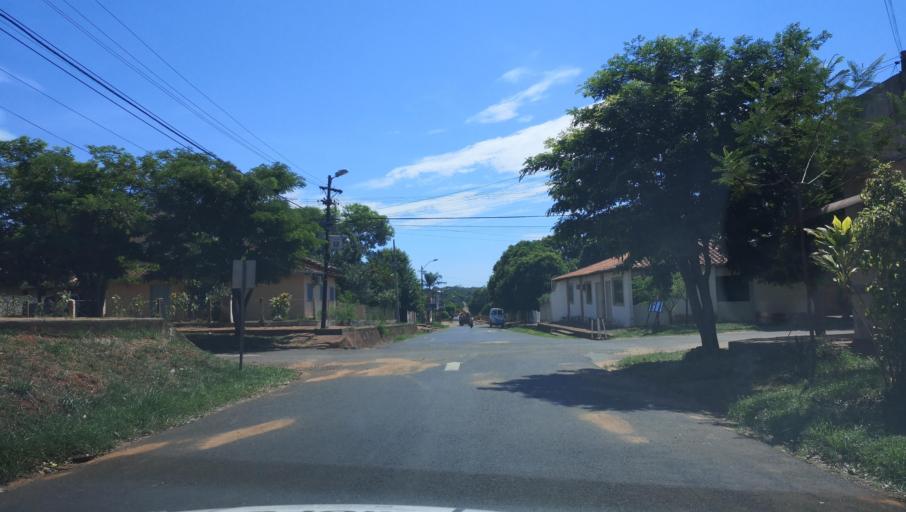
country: PY
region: Misiones
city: Santa Maria
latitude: -26.8894
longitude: -57.0292
